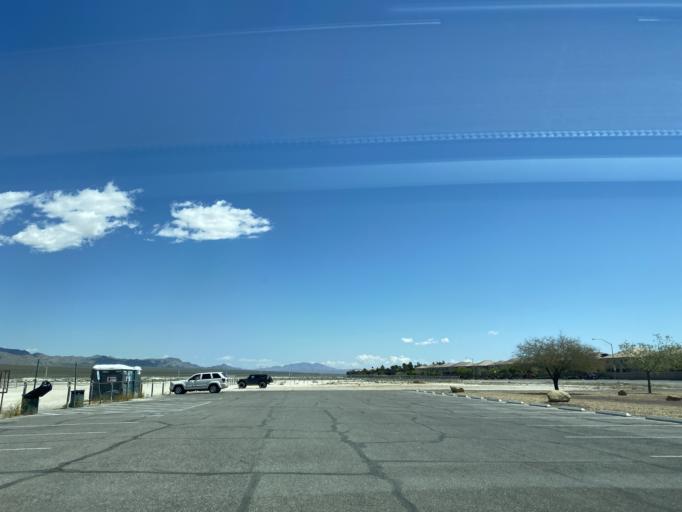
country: US
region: Nevada
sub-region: Clark County
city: North Las Vegas
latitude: 36.3140
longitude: -115.1988
